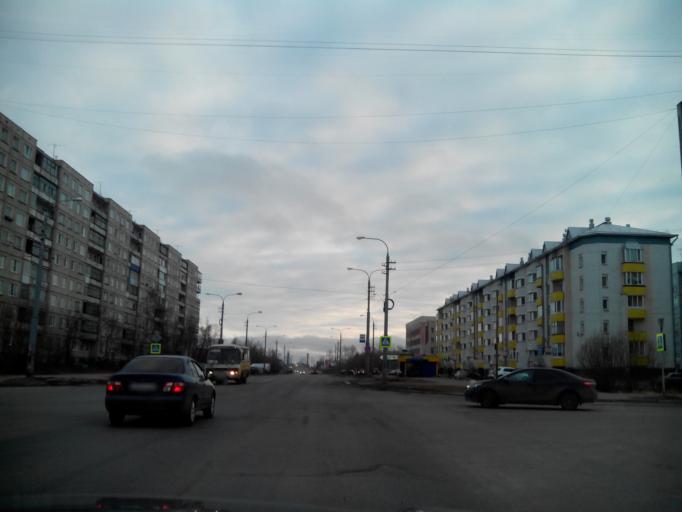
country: RU
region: Arkhangelskaya
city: Arkhangel'sk
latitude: 64.5151
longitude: 40.6708
